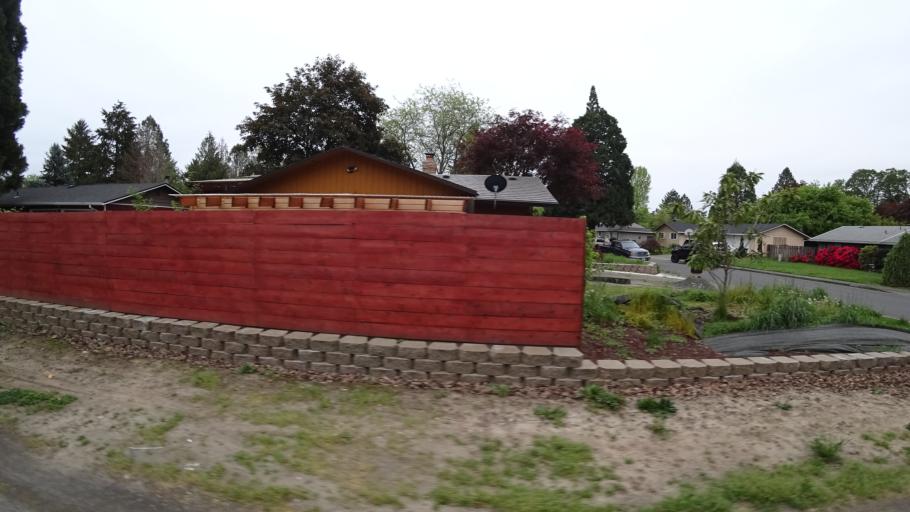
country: US
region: Oregon
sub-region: Washington County
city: Aloha
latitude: 45.5078
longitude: -122.8831
